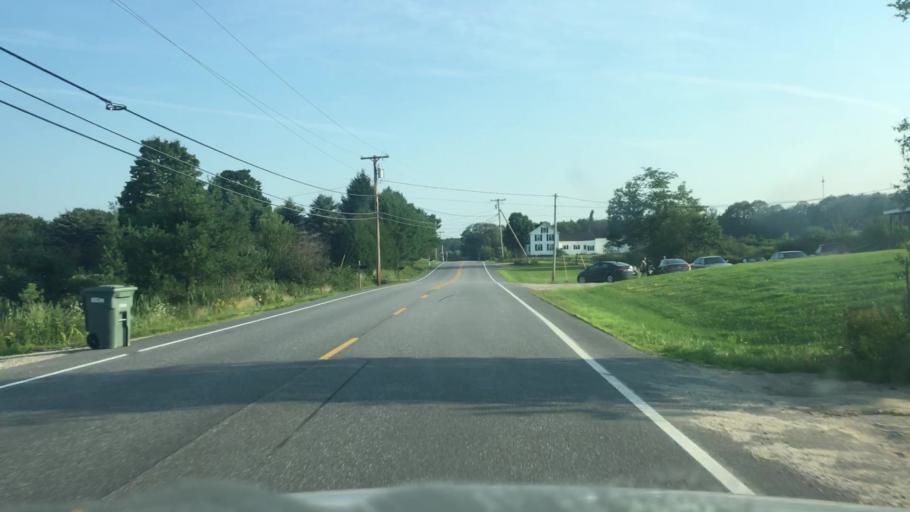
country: US
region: Maine
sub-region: Cumberland County
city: Freeport
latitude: 43.8998
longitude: -70.0939
